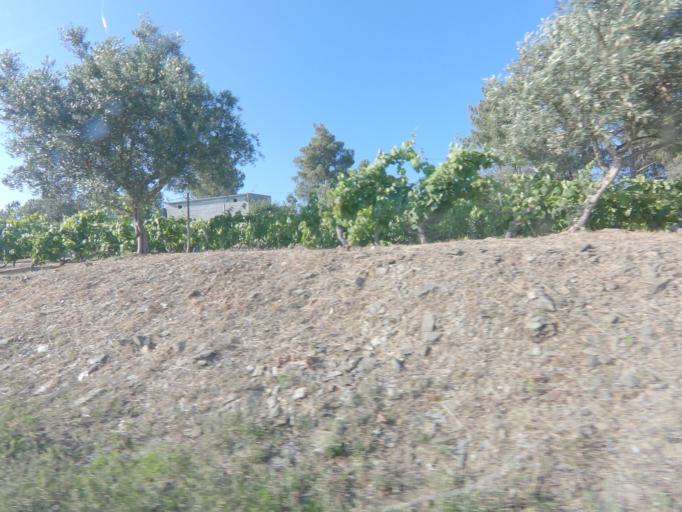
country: PT
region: Vila Real
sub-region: Sabrosa
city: Vilela
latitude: 41.1779
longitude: -7.6077
